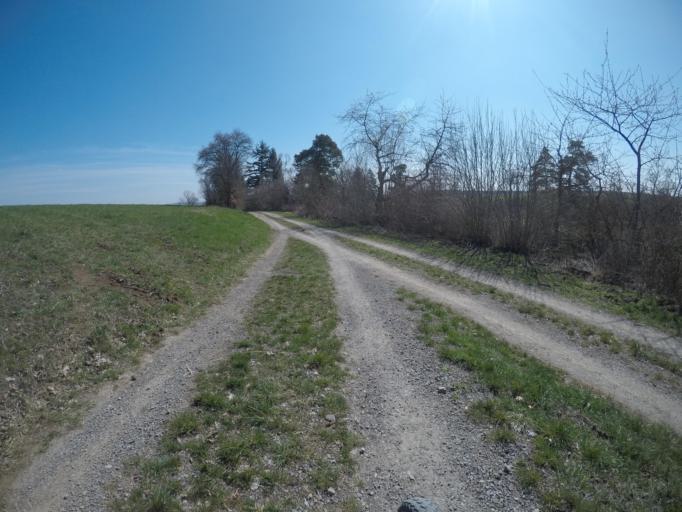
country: DE
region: Baden-Wuerttemberg
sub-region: Regierungsbezirk Stuttgart
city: Herrenberg
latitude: 48.5884
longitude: 8.8245
